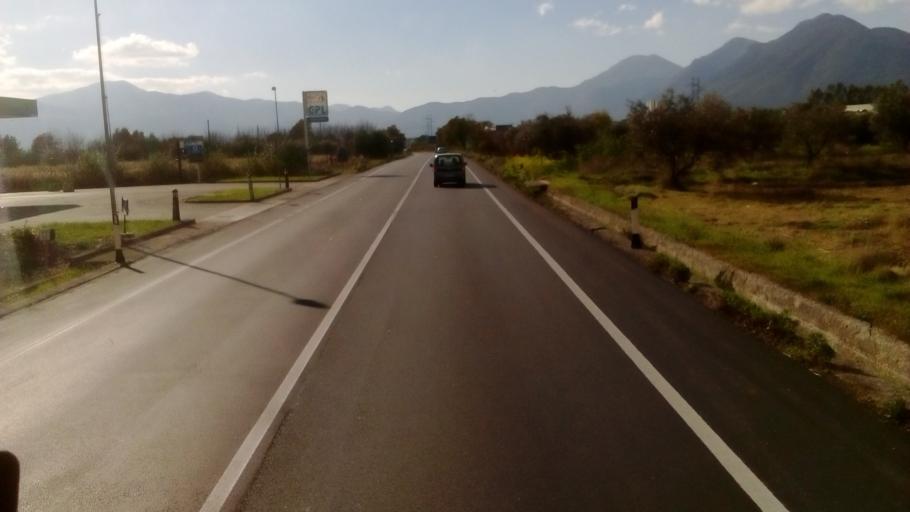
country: IT
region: Molise
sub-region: Provincia di Isernia
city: Taverna Ravindola
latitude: 41.5139
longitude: 14.1191
